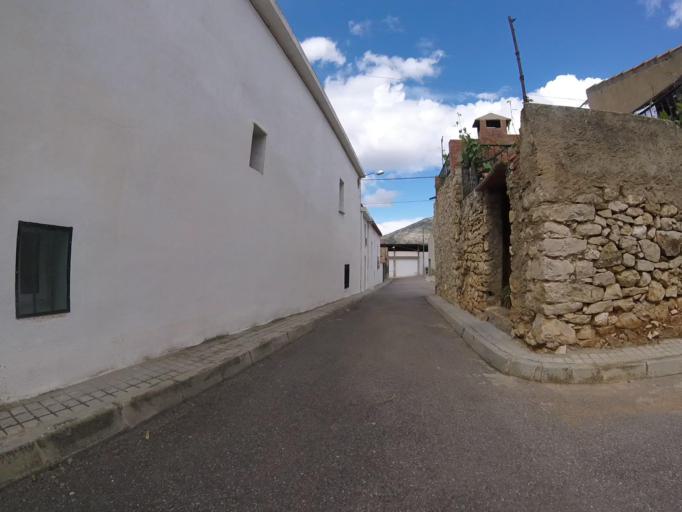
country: ES
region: Valencia
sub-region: Provincia de Castello
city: Sierra-Engarceran
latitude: 40.2930
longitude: -0.0451
